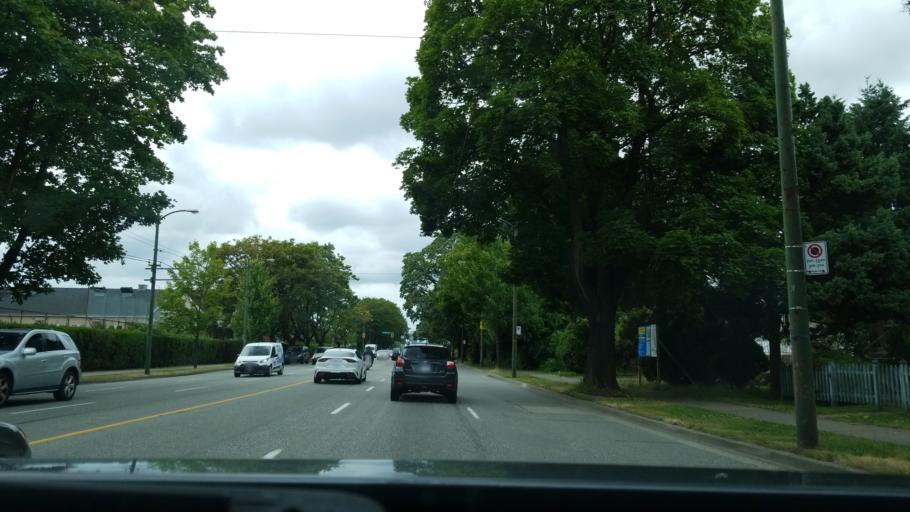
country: CA
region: British Columbia
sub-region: Fraser Valley Regional District
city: North Vancouver
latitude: 49.2623
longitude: -123.0594
